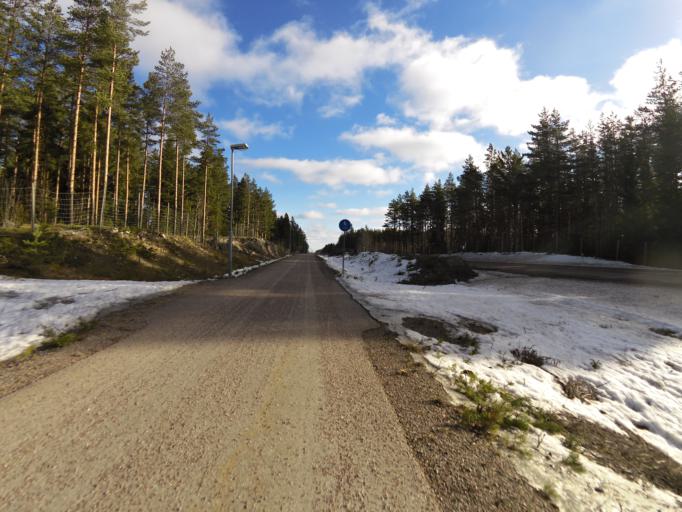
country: SE
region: Uppsala
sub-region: Alvkarleby Kommun
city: Skutskaer
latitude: 60.6461
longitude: 17.2766
